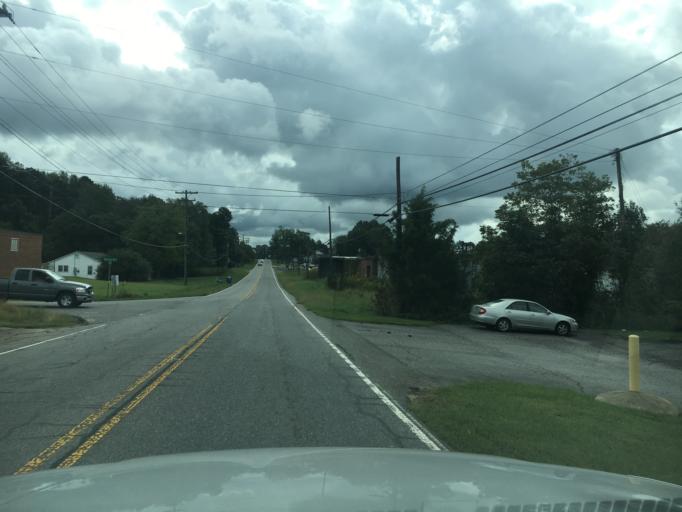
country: US
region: North Carolina
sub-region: Catawba County
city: Saint Stephens
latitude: 35.7258
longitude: -81.2684
